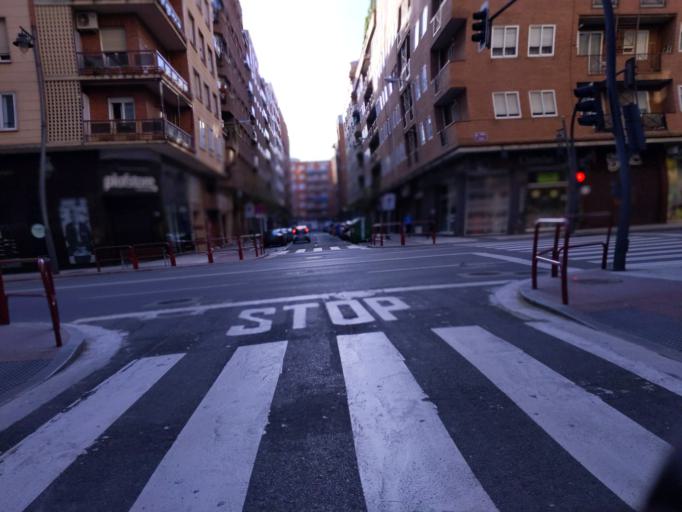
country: ES
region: La Rioja
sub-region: Provincia de La Rioja
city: Logrono
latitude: 42.4642
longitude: -2.4533
